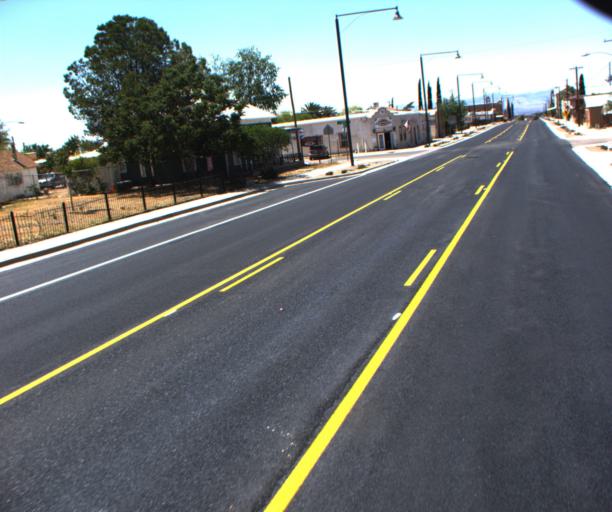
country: US
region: Arizona
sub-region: Cochise County
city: Tombstone
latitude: 31.7127
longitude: -110.0639
